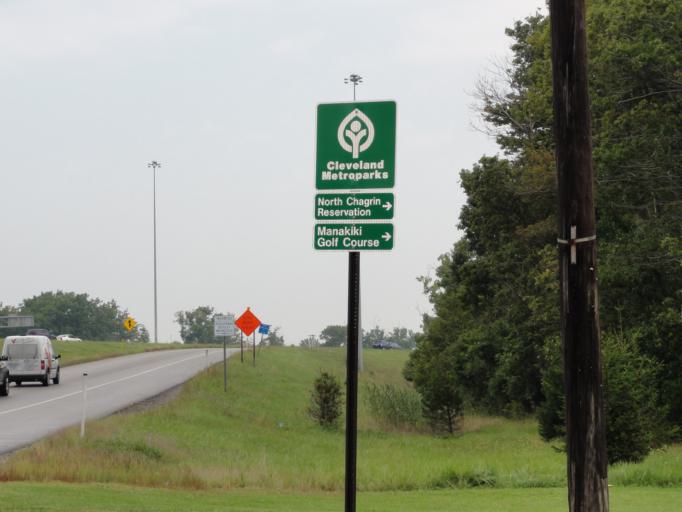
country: US
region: Ohio
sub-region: Cuyahoga County
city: Mayfield
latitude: 41.5390
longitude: -81.4498
